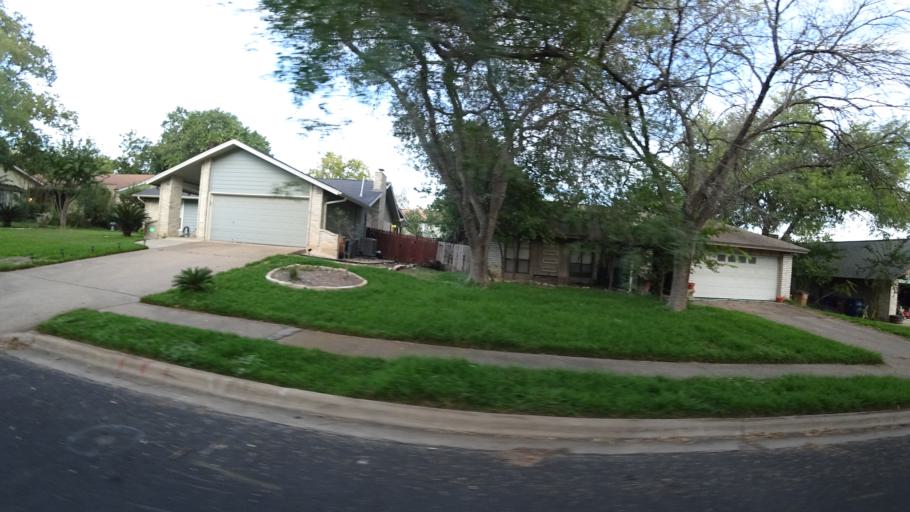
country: US
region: Texas
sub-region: Travis County
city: Austin
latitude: 30.2047
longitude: -97.7646
